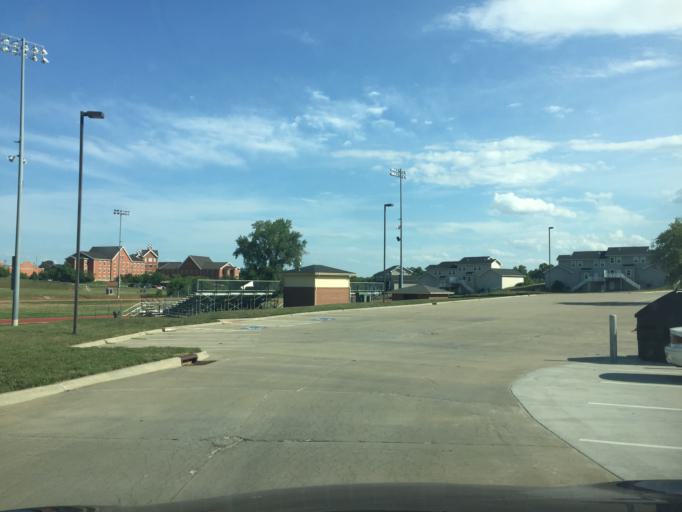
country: US
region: Kansas
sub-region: Leavenworth County
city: Leavenworth
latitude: 39.3458
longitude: -94.9302
